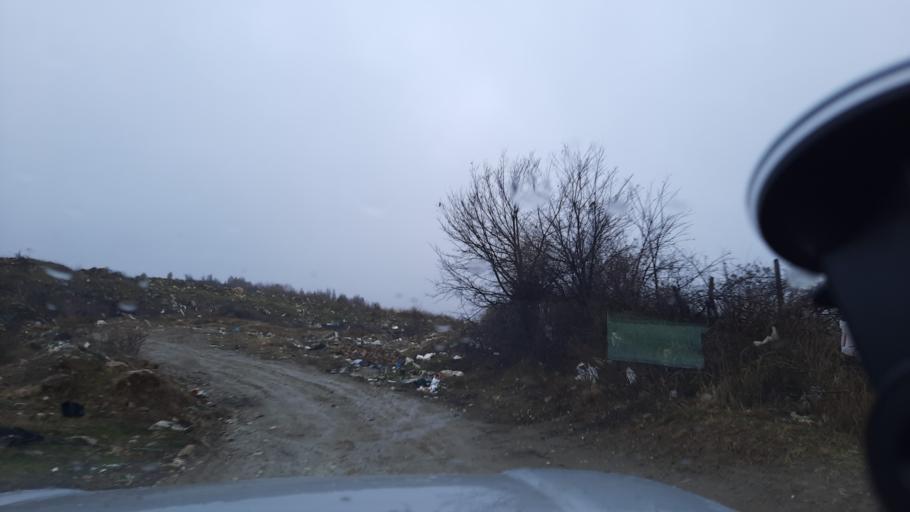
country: MK
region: Opstina Lipkovo
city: Matejche
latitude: 42.1254
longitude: 21.5853
